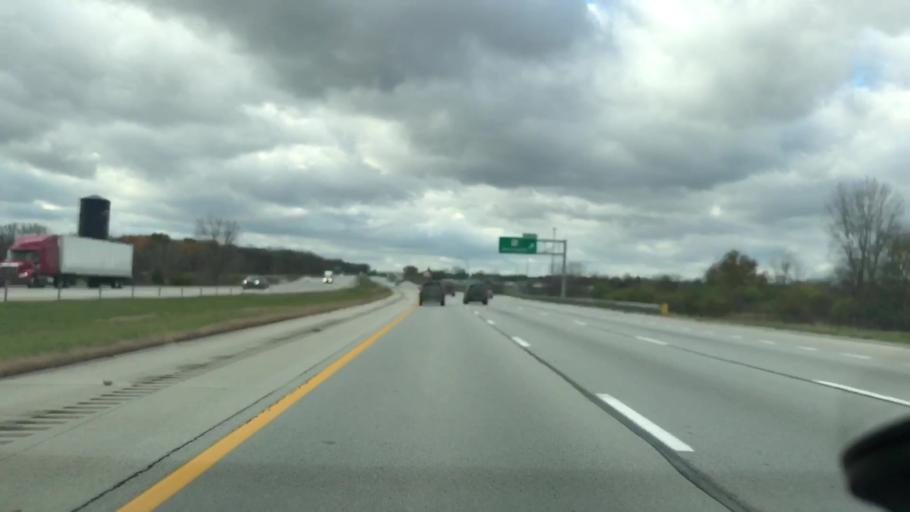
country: US
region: Ohio
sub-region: Clark County
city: Lisbon
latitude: 39.9260
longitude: -83.6821
